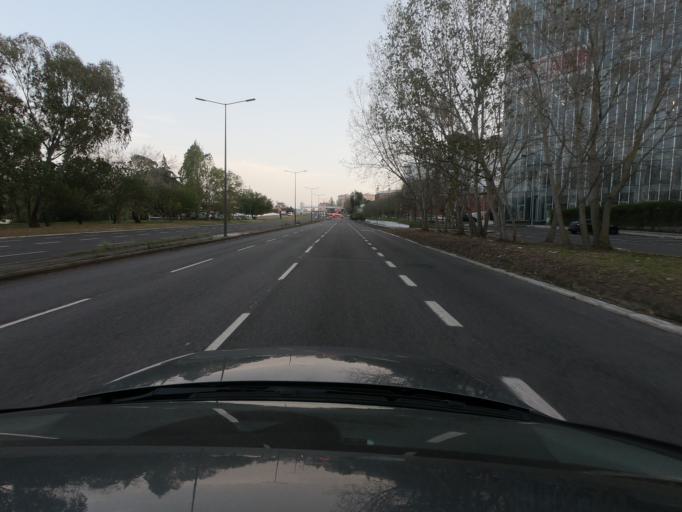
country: PT
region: Lisbon
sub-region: Odivelas
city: Olival do Basto
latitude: 38.7702
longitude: -9.1643
